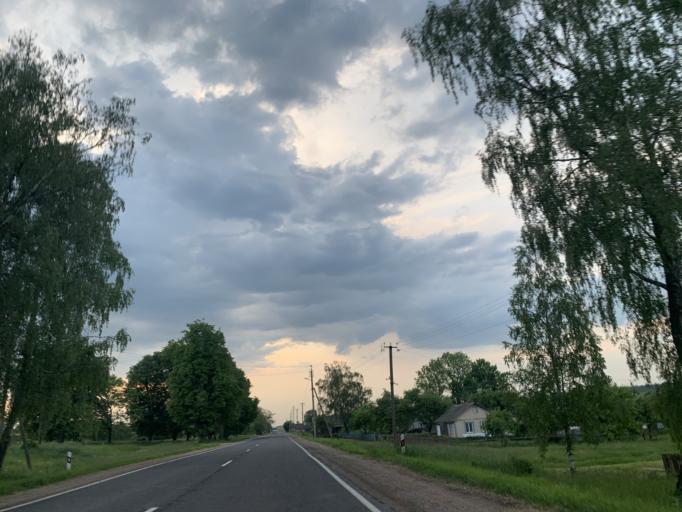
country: BY
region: Minsk
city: Tsimkavichy
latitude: 53.1300
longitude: 26.8773
